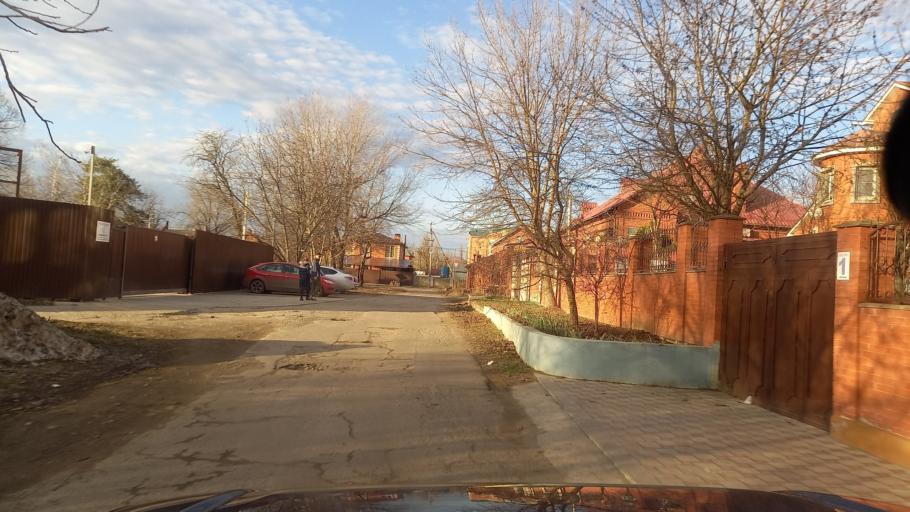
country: RU
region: Krasnodarskiy
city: Pashkovskiy
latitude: 45.0123
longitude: 39.1064
